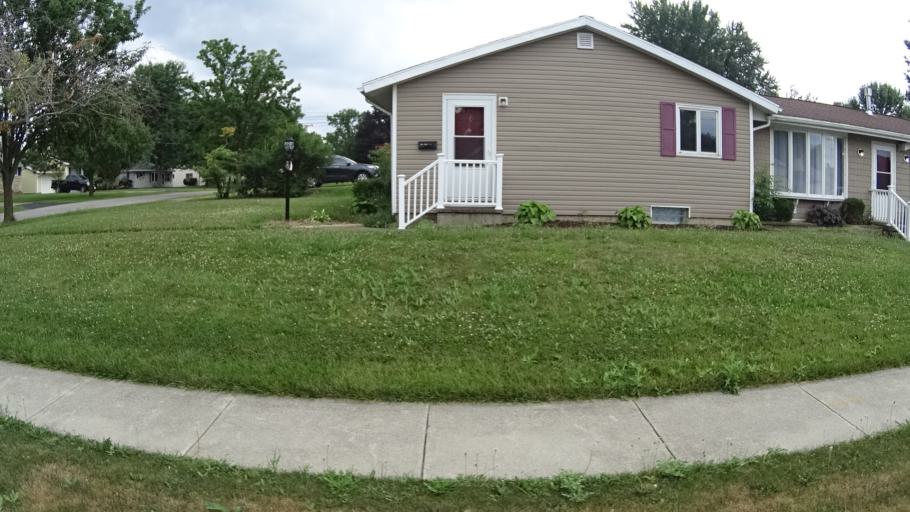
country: US
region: Ohio
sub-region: Erie County
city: Sandusky
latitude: 41.4403
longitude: -82.7644
